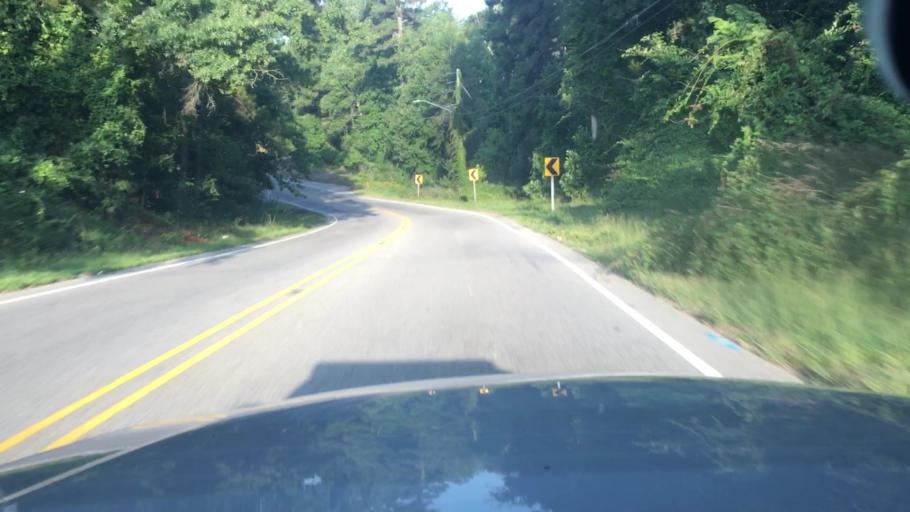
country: US
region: North Carolina
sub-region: Cumberland County
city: Spring Lake
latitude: 35.1078
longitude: -78.9420
